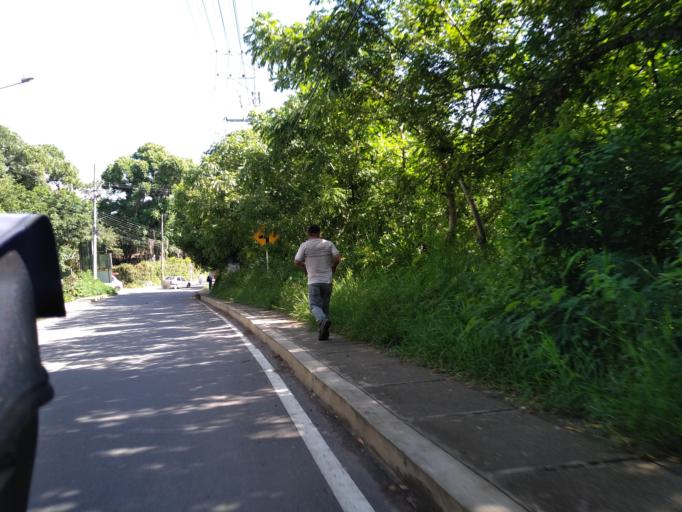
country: CO
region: Santander
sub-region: San Gil
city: San Gil
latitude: 6.5462
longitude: -73.1282
